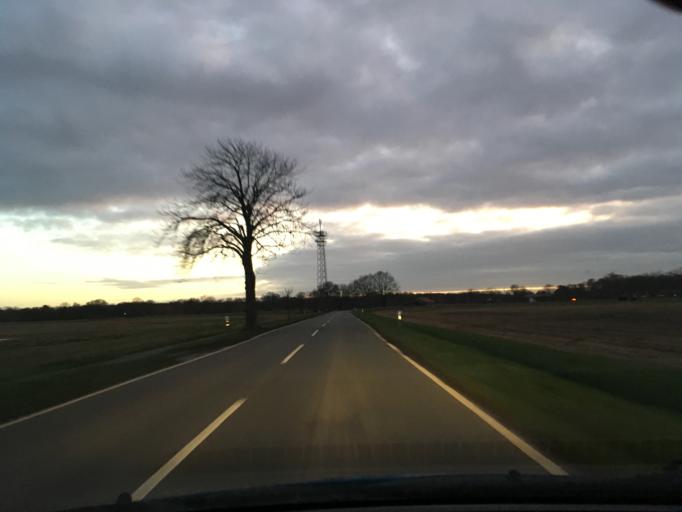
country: DE
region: Lower Saxony
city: Barum
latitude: 53.3599
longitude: 10.4111
